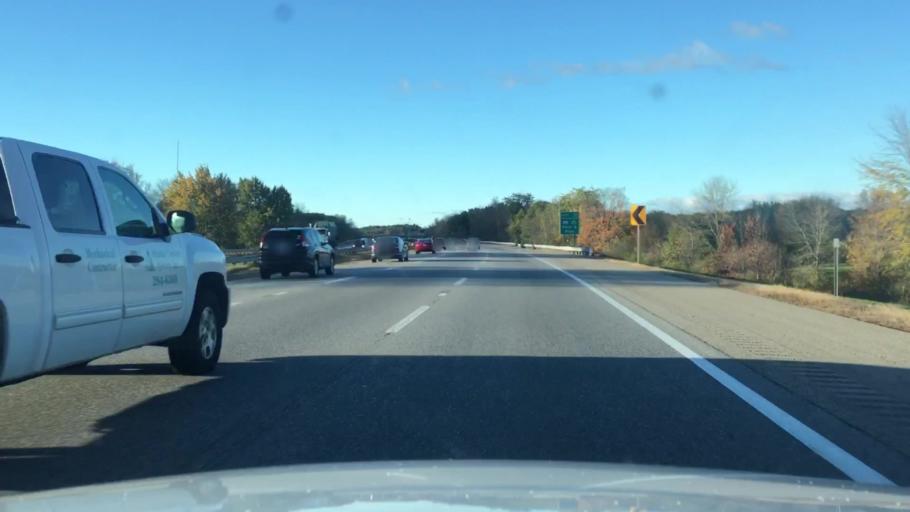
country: US
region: Maine
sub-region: York County
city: Biddeford
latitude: 43.5023
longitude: -70.4858
